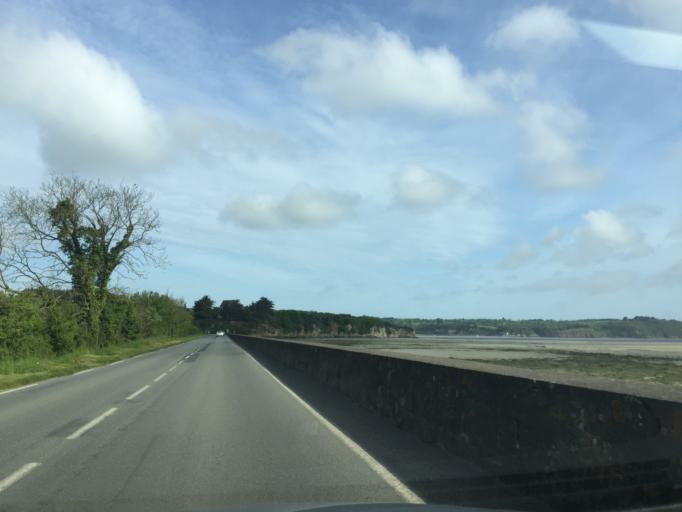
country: FR
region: Brittany
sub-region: Departement des Cotes-d'Armor
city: Matignon
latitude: 48.6109
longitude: -2.3173
